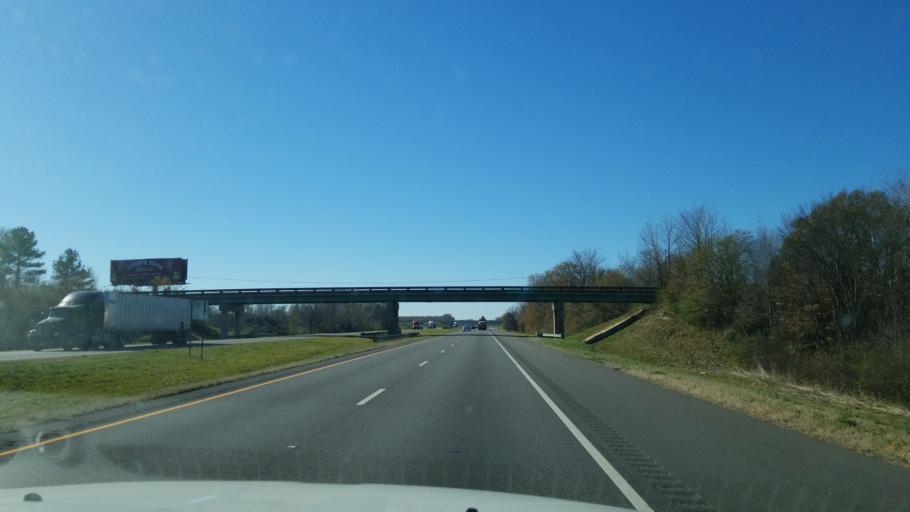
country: US
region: Alabama
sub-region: Tuscaloosa County
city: Tuscaloosa
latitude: 33.1561
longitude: -87.5871
